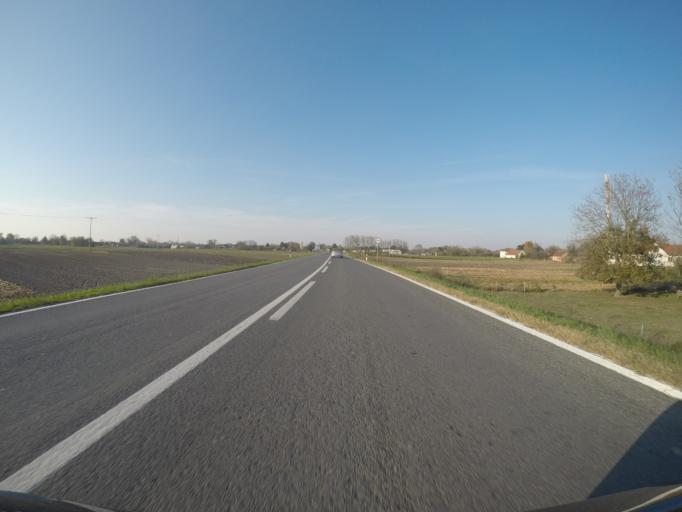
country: HU
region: Somogy
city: Barcs
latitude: 45.9362
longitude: 17.4615
